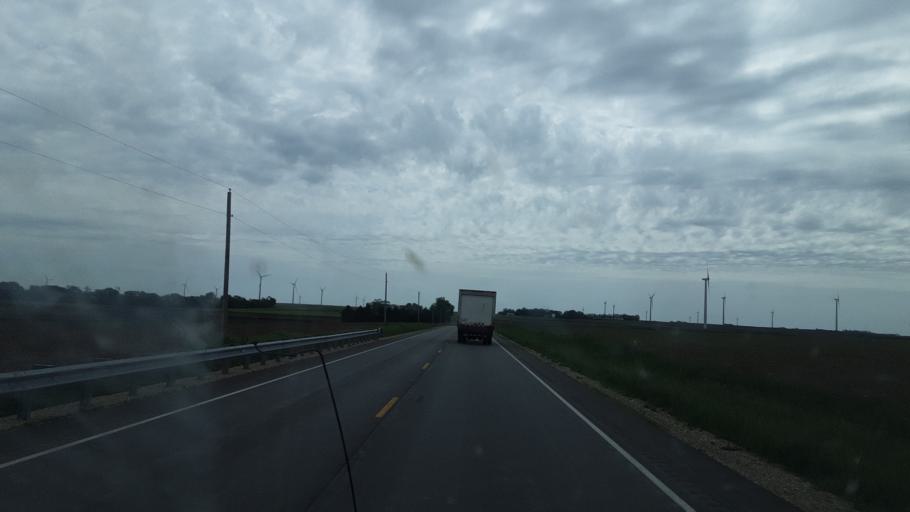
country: US
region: Illinois
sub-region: Tazewell County
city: Richmond
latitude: 40.3086
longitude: -89.4316
